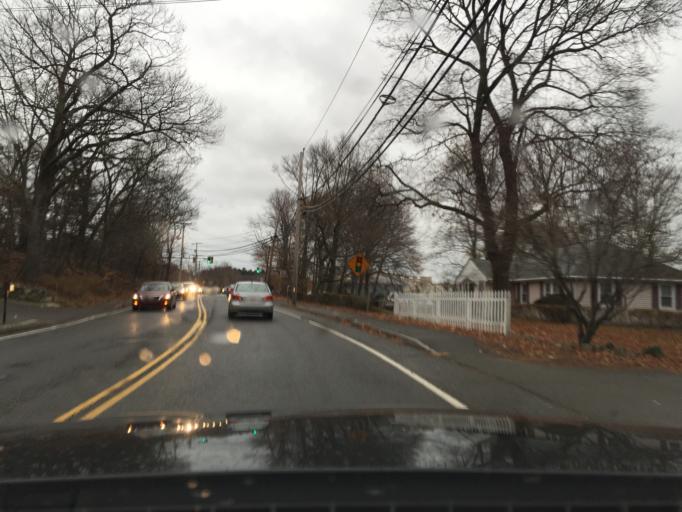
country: US
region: Massachusetts
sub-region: Essex County
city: Saugus
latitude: 42.4916
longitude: -71.0196
